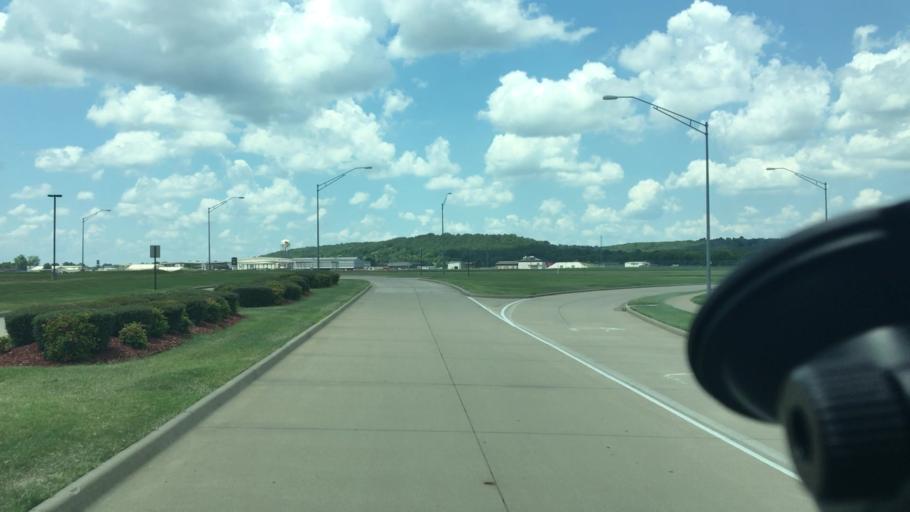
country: US
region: Arkansas
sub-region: Sebastian County
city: Fort Smith
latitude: 35.3428
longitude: -94.3591
